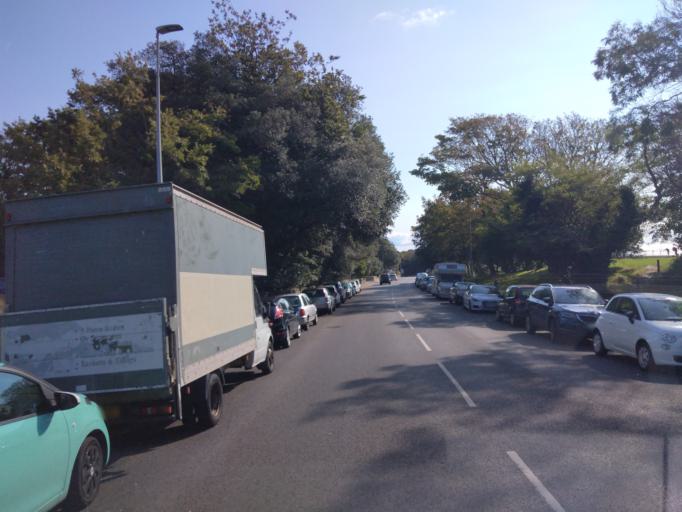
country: GB
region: England
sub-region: East Sussex
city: Hastings
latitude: 50.8578
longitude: 0.5668
